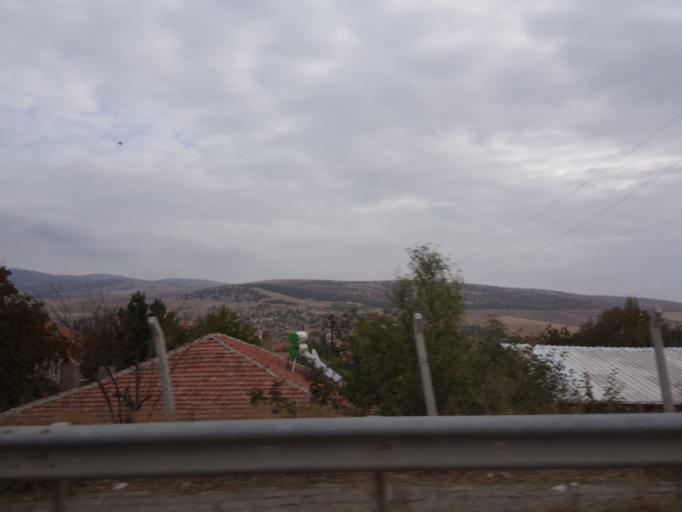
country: TR
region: Kirikkale
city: Keskin
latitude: 39.6695
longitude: 33.6112
